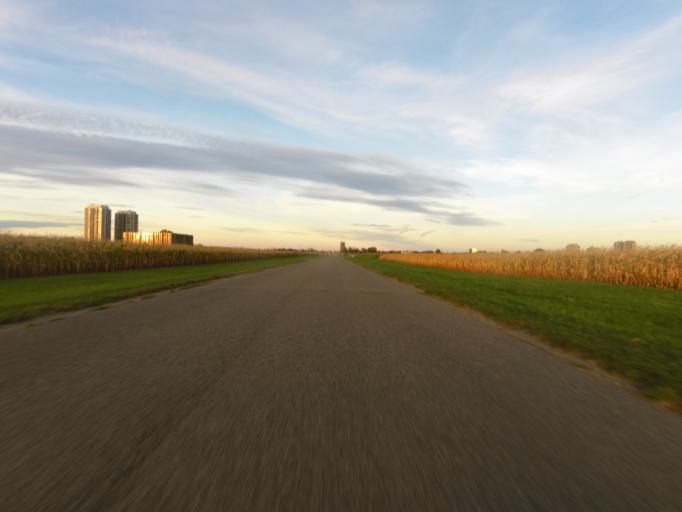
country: CA
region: Ontario
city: Ottawa
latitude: 45.3727
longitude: -75.7246
